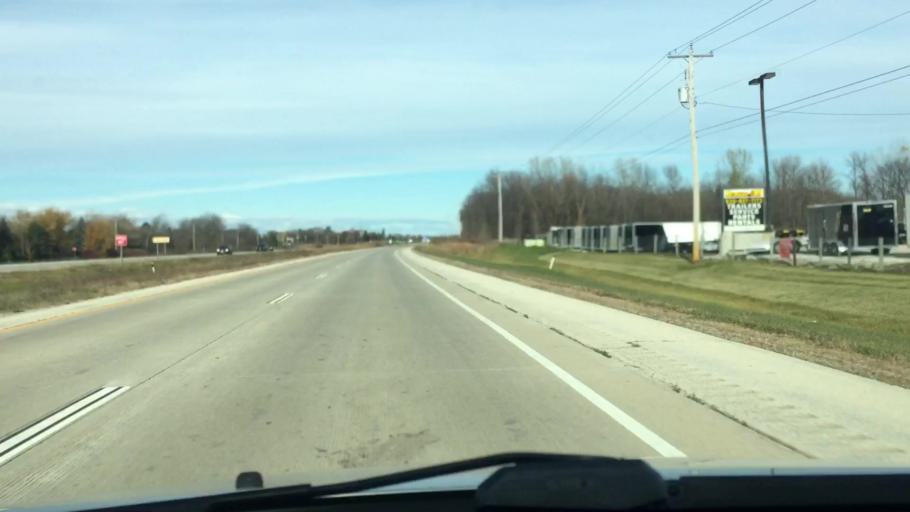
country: US
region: Wisconsin
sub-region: Brown County
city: Bellevue
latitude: 44.5684
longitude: -87.8781
